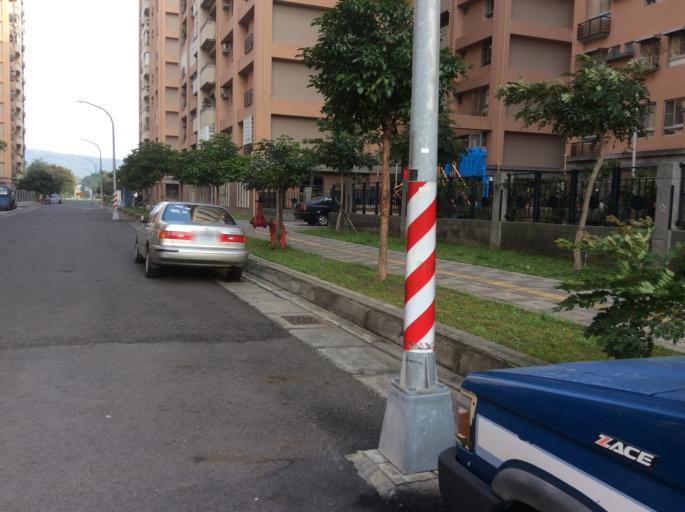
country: TW
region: Kaohsiung
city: Kaohsiung
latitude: 22.6968
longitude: 120.2869
